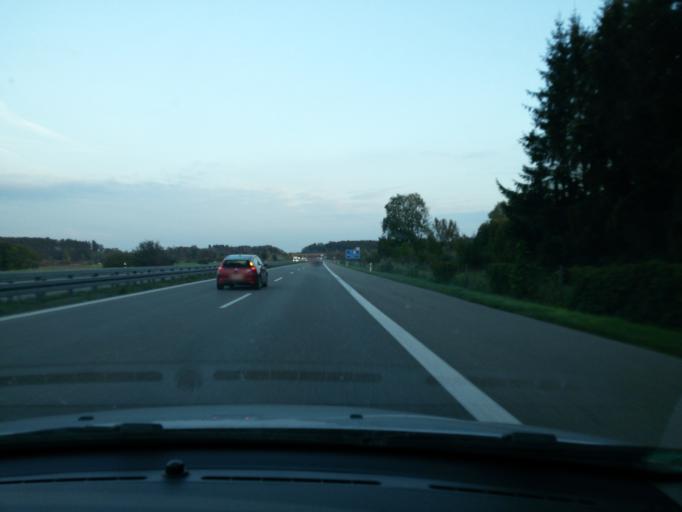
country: DE
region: Bavaria
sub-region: Swabia
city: Wiedergeltingen
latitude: 48.0347
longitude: 10.6531
